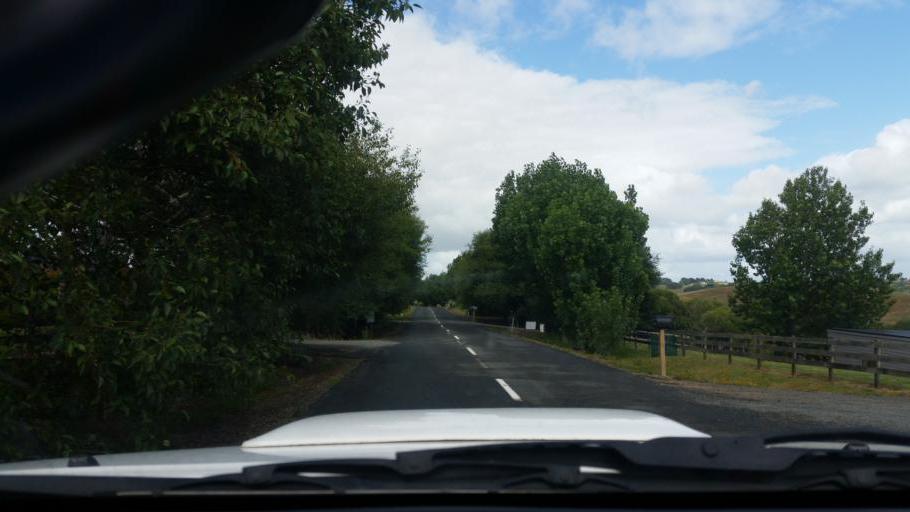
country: NZ
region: Auckland
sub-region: Auckland
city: Wellsford
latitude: -36.1307
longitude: 174.3694
